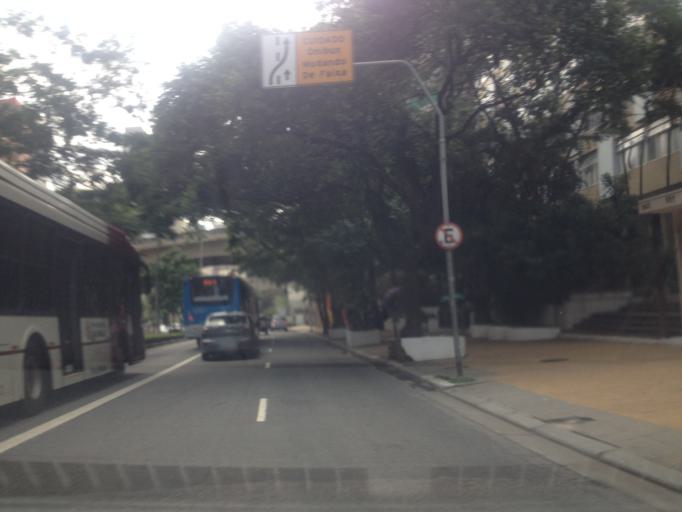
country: BR
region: Sao Paulo
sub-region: Sao Paulo
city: Sao Paulo
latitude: -23.5506
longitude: -46.6441
